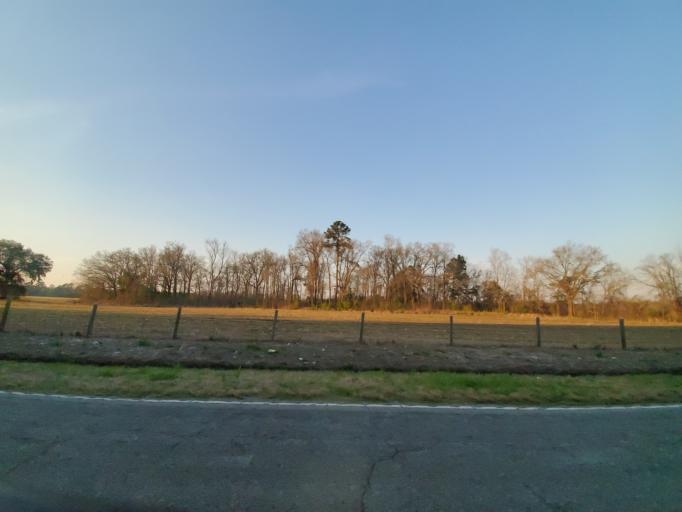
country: US
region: South Carolina
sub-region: Dorchester County
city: Saint George
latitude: 33.0457
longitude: -80.5858
